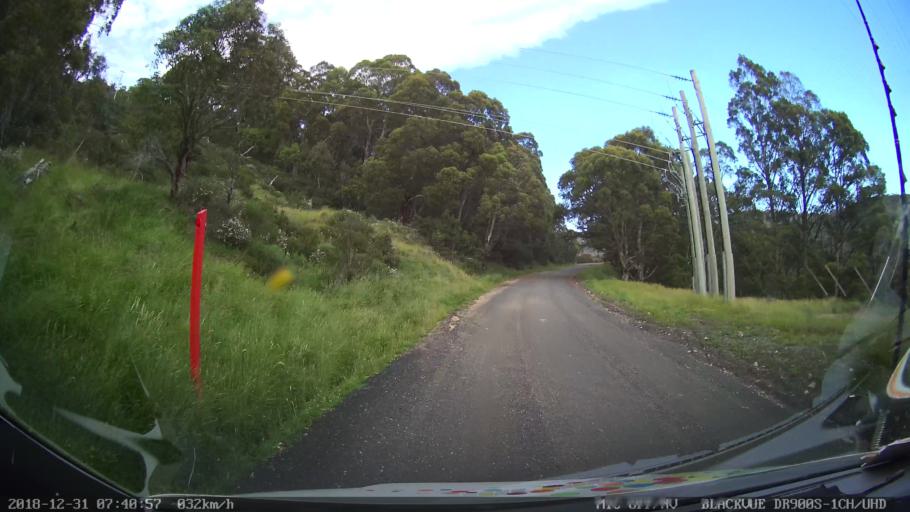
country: AU
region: New South Wales
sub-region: Snowy River
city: Jindabyne
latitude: -36.3528
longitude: 148.4150
